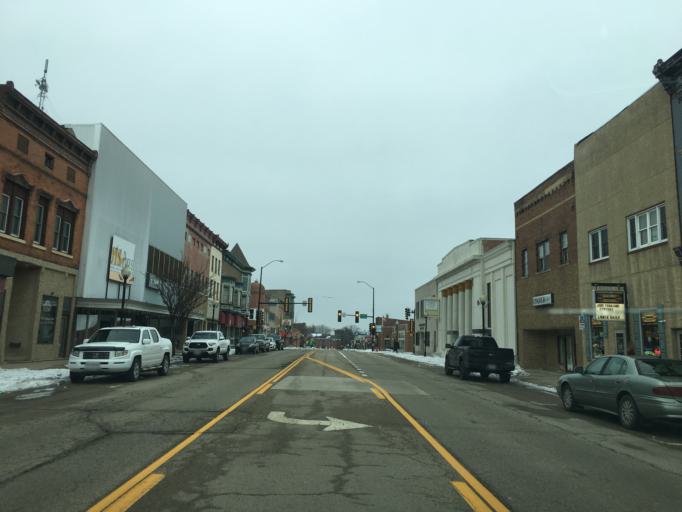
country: US
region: Illinois
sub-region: LaSalle County
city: Peru
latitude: 41.3276
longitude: -89.1303
